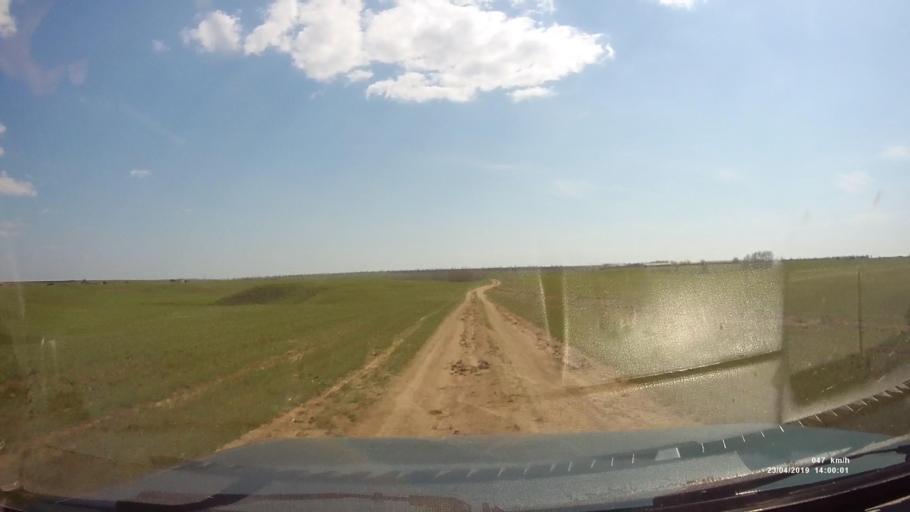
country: RU
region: Rostov
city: Remontnoye
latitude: 46.5625
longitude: 42.9468
